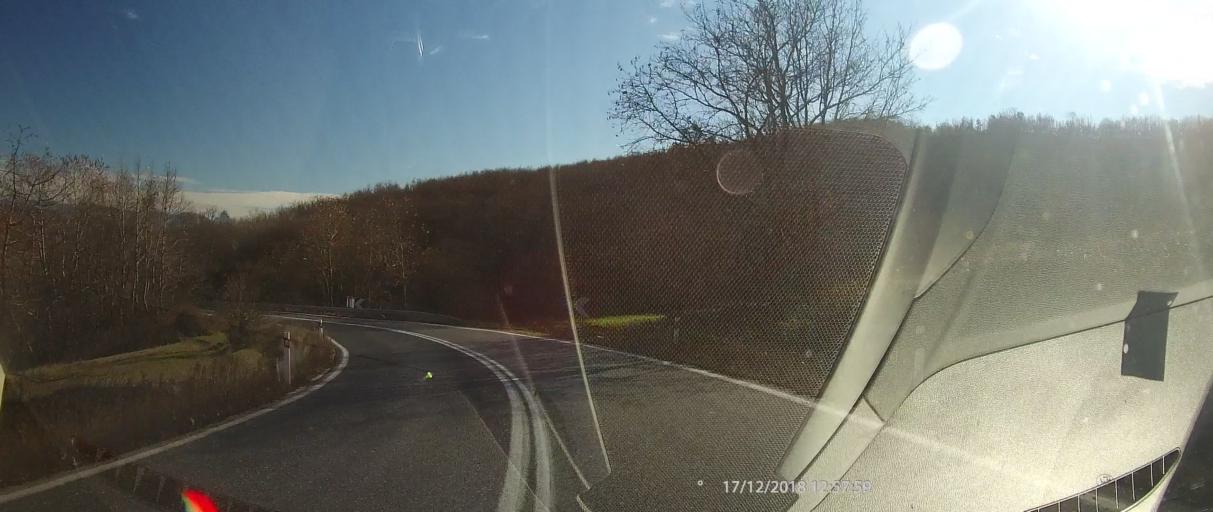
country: GR
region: Thessaly
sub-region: Trikala
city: Kastraki
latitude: 39.7425
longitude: 21.5363
